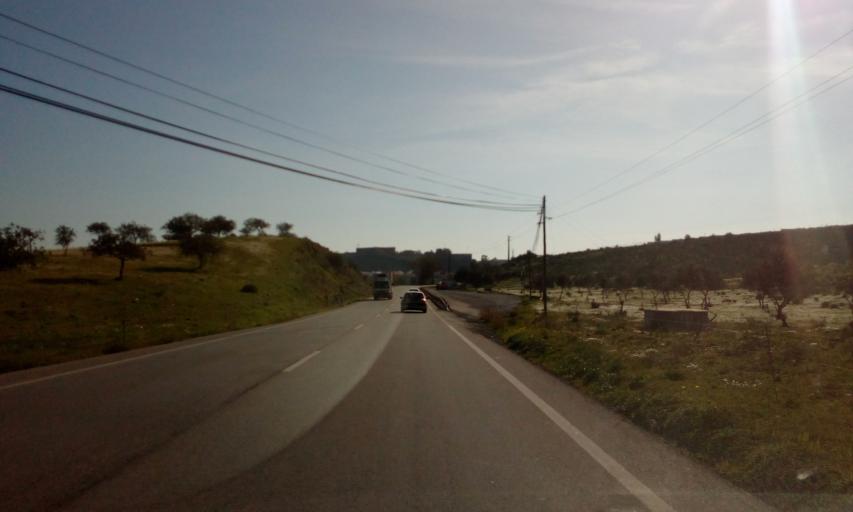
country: PT
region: Faro
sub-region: Castro Marim
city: Castro Marim
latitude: 37.2263
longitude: -7.4467
